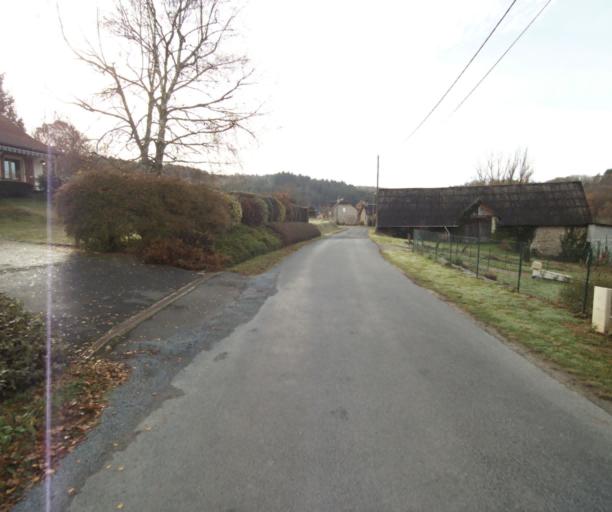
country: FR
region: Limousin
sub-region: Departement de la Correze
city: Chameyrat
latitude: 45.2245
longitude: 1.7227
